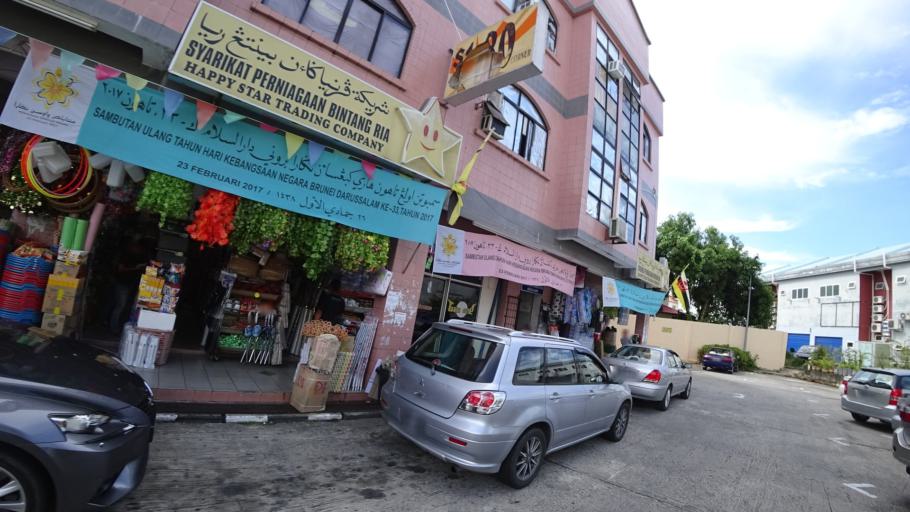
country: BN
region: Brunei and Muara
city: Bandar Seri Begawan
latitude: 4.8881
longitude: 114.8403
